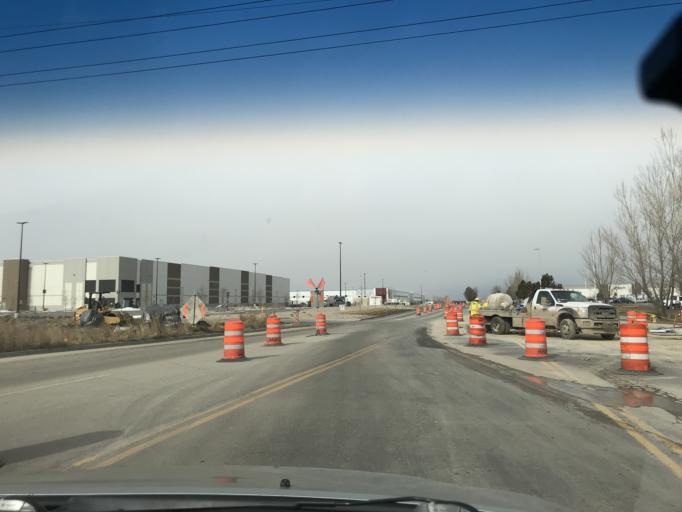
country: US
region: Utah
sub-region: Salt Lake County
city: West Valley City
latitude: 40.7838
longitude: -112.0250
